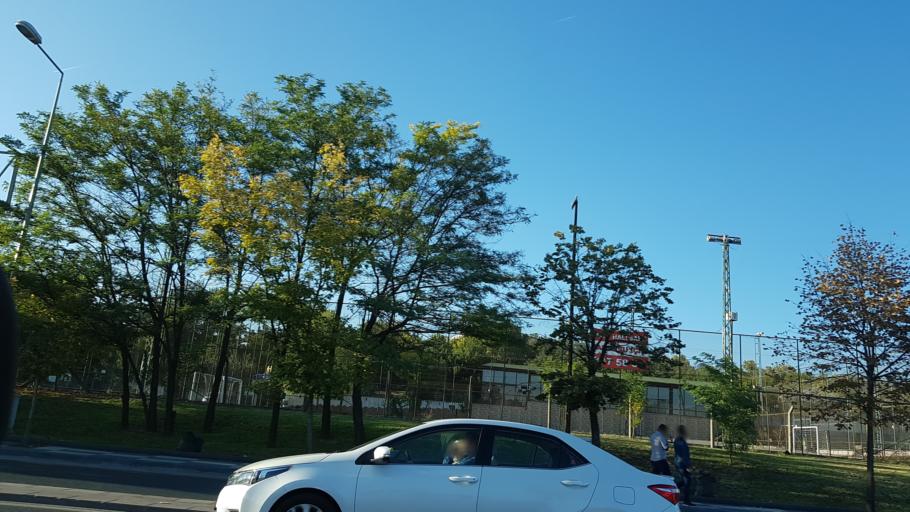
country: TR
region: Ankara
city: Batikent
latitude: 39.9472
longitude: 32.7838
